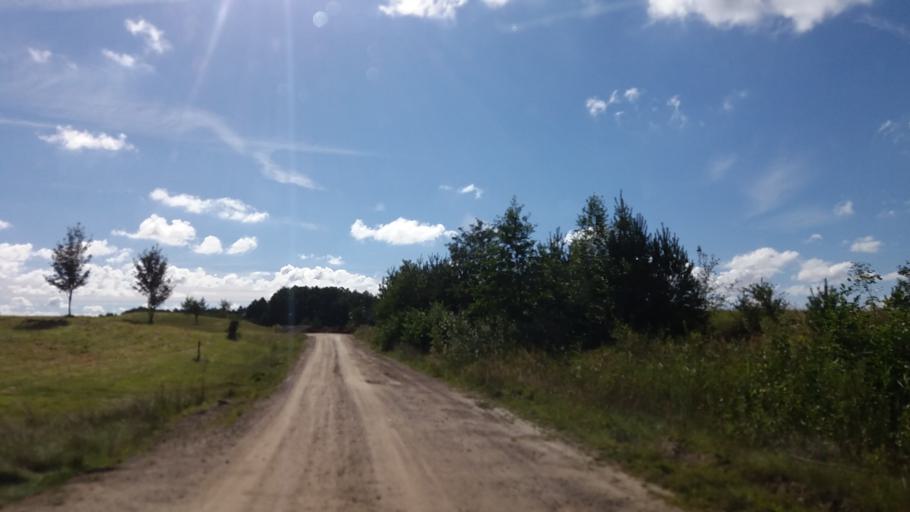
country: PL
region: West Pomeranian Voivodeship
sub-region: Powiat choszczenski
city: Krzecin
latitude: 53.1328
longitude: 15.4888
